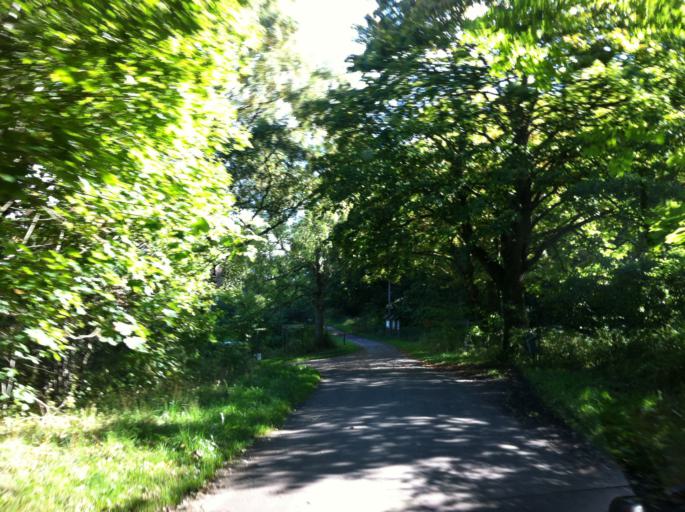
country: SE
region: Skane
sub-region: Kristianstads Kommun
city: Degeberga
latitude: 55.7359
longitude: 13.9371
